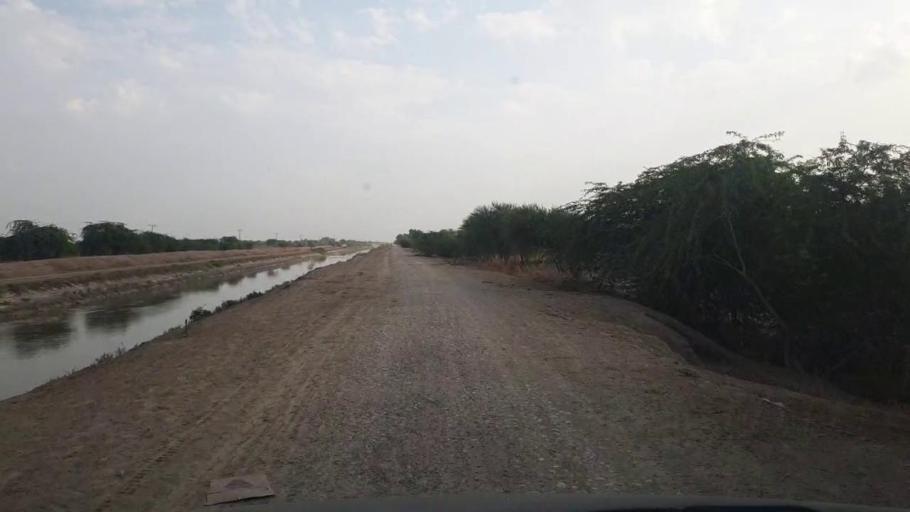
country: PK
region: Sindh
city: Badin
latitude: 24.5240
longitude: 68.6810
